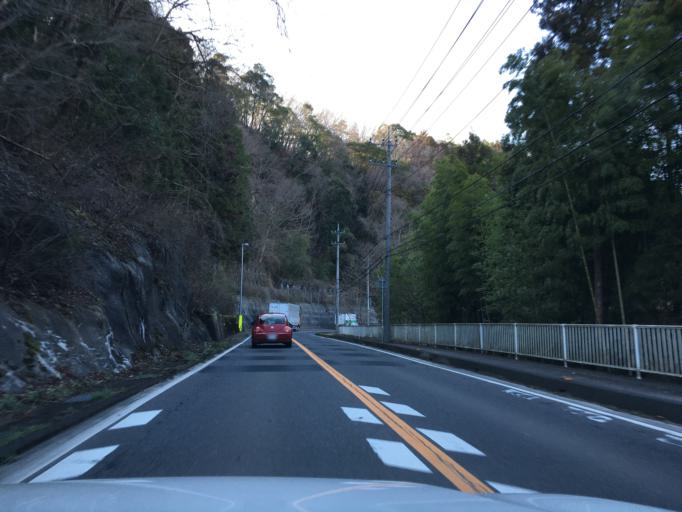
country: JP
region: Ibaraki
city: Daigo
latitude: 36.7514
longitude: 140.3836
